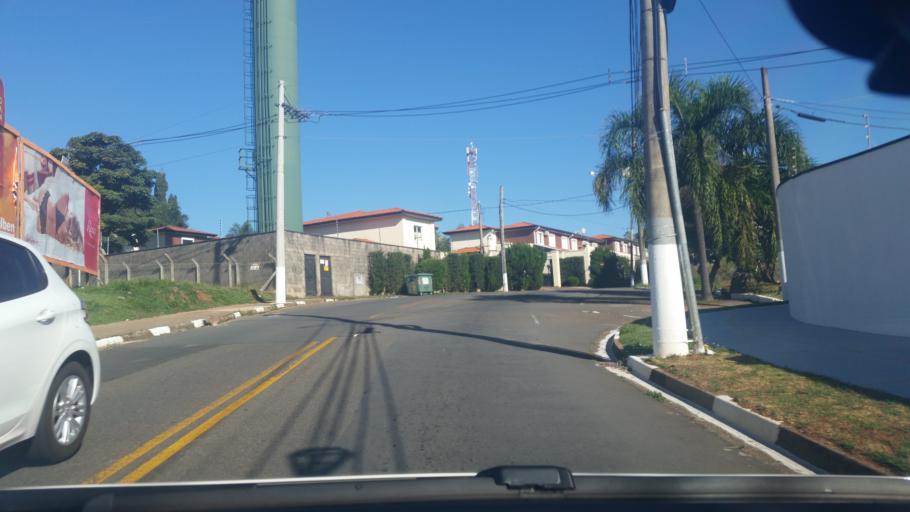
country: BR
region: Sao Paulo
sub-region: Campinas
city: Campinas
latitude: -22.8597
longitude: -47.0540
